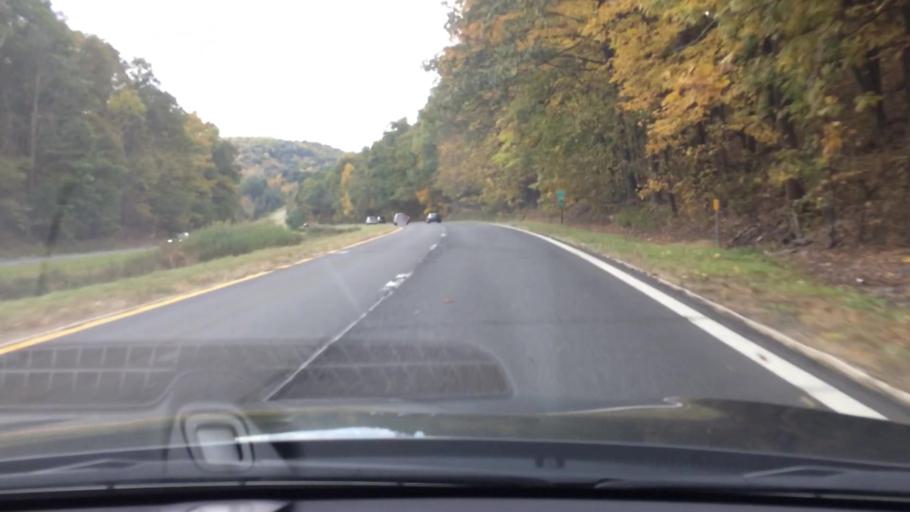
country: US
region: New York
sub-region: Dutchess County
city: Hillside Lake
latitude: 41.6802
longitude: -73.7875
